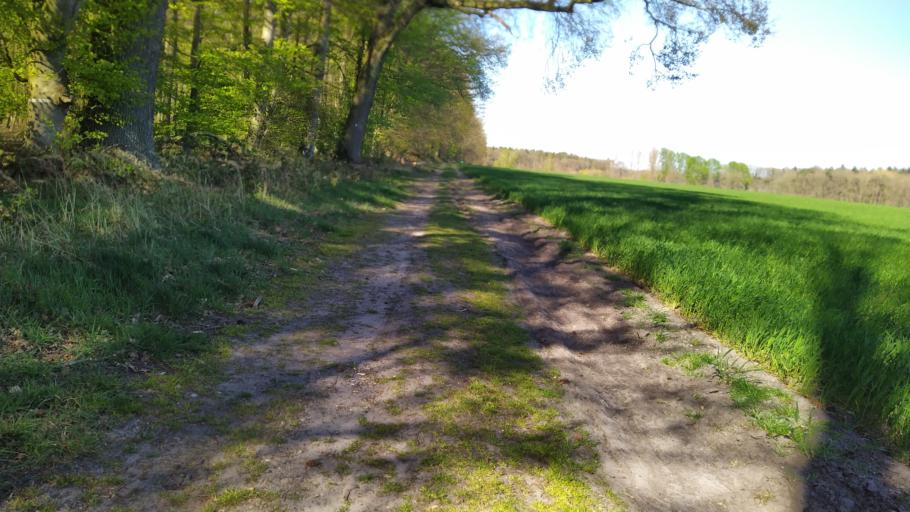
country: DE
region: Lower Saxony
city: Klein Meckelsen
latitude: 53.2960
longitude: 9.4287
